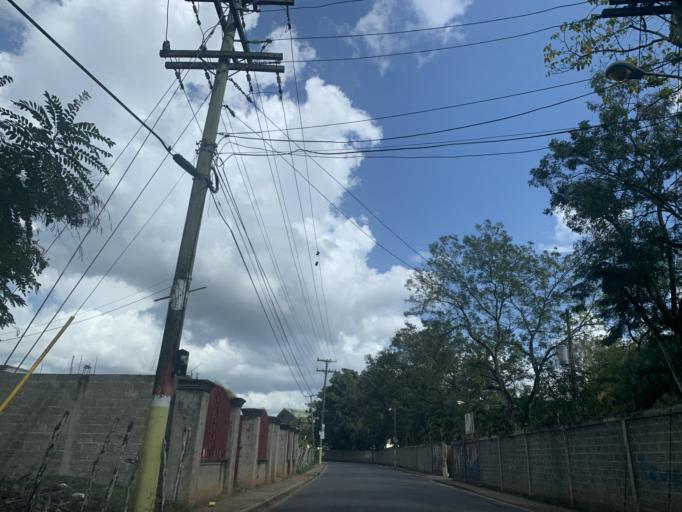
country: DO
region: Monte Plata
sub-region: Yamasa
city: Yamasa
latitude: 18.7708
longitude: -70.0177
